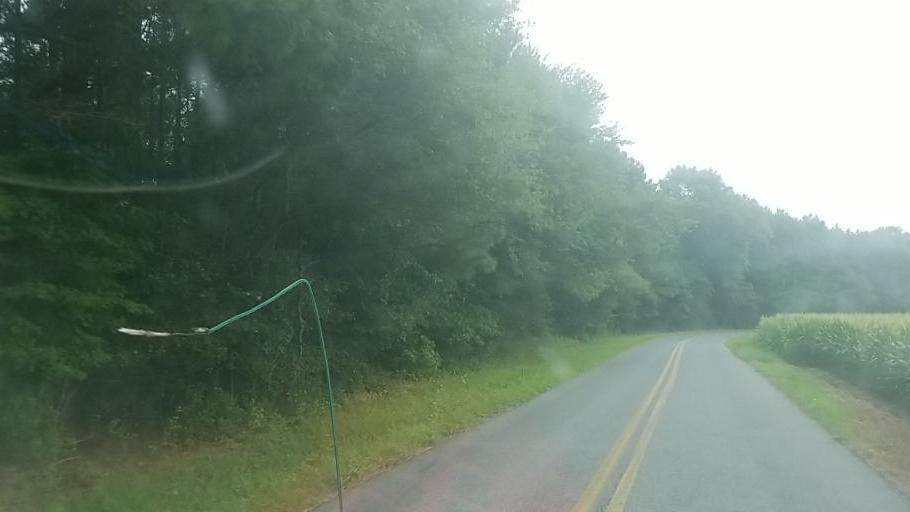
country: US
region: Delaware
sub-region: Sussex County
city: Selbyville
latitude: 38.4241
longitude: -75.3066
